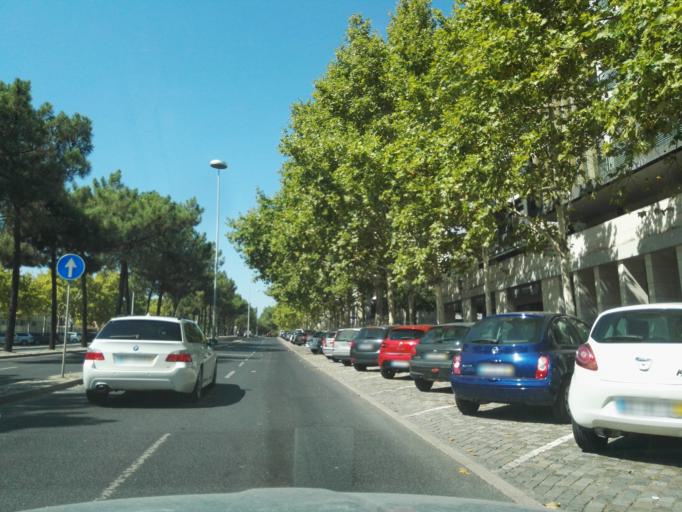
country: PT
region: Lisbon
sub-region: Loures
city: Moscavide
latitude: 38.7787
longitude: -9.0975
